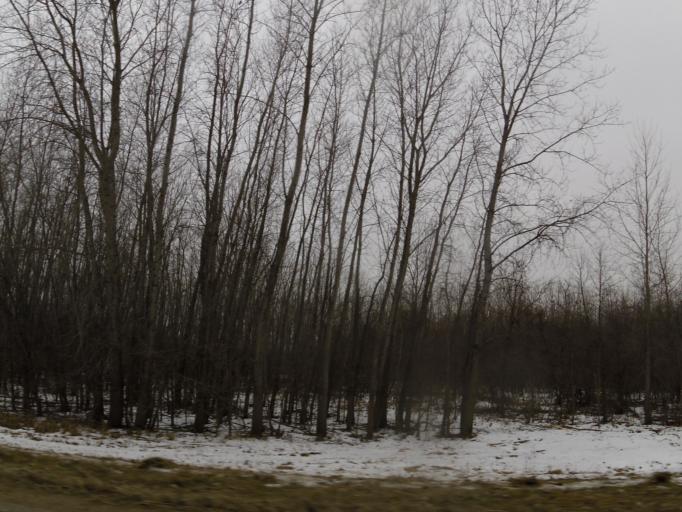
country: US
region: Minnesota
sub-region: Scott County
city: Jordan
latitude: 44.6964
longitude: -93.6438
